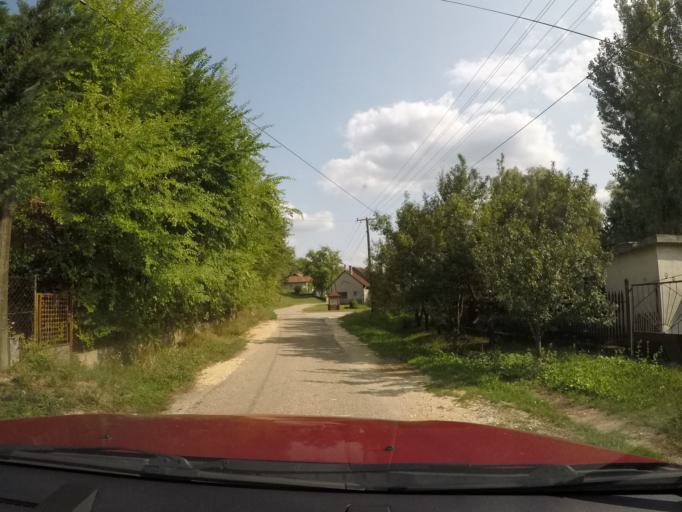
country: HU
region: Borsod-Abauj-Zemplen
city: Szendro
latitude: 48.5205
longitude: 20.6815
